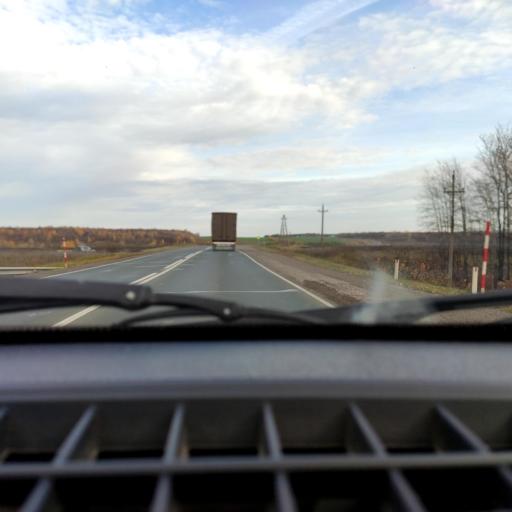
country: RU
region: Bashkortostan
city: Avdon
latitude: 54.7246
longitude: 55.7771
